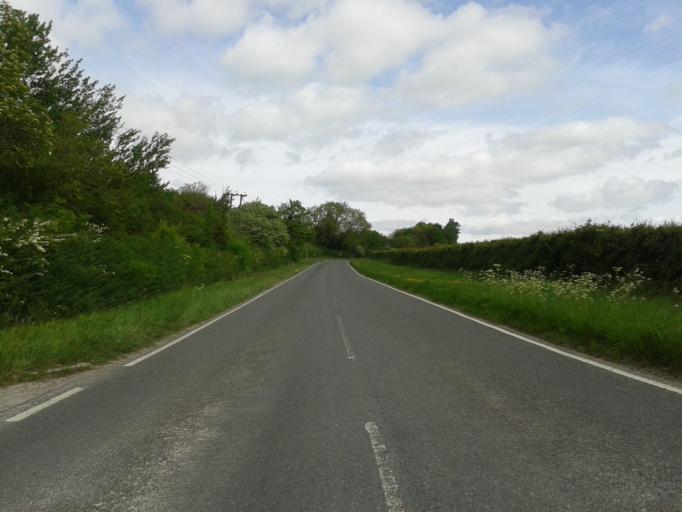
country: GB
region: England
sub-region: Cambridgeshire
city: Haslingfield
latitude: 52.1383
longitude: 0.0422
